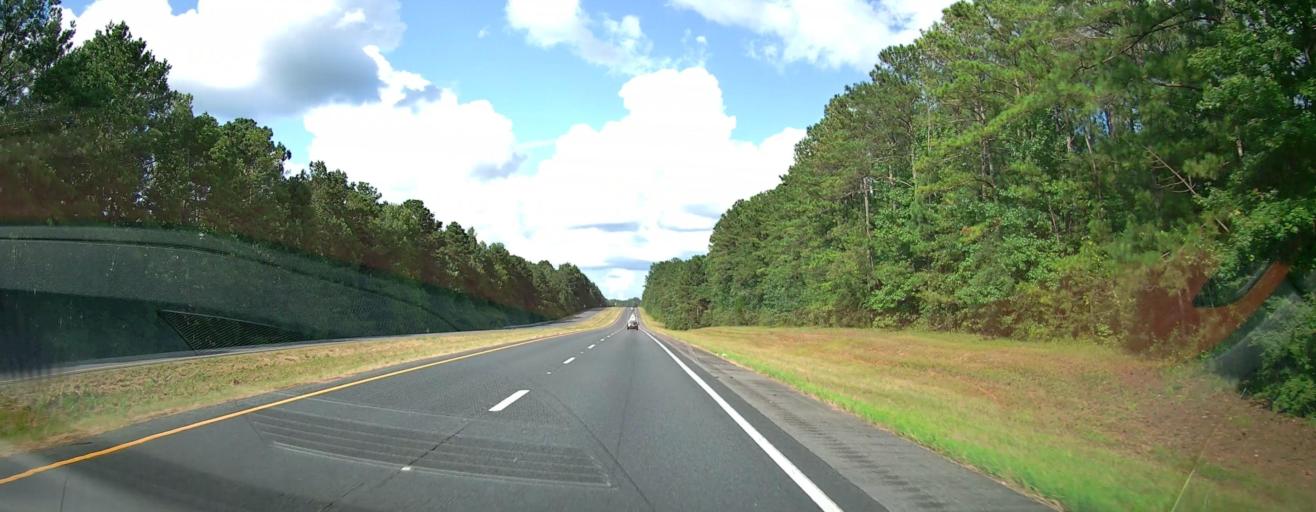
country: US
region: Georgia
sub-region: Muscogee County
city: Columbus
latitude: 32.5649
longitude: -84.8305
